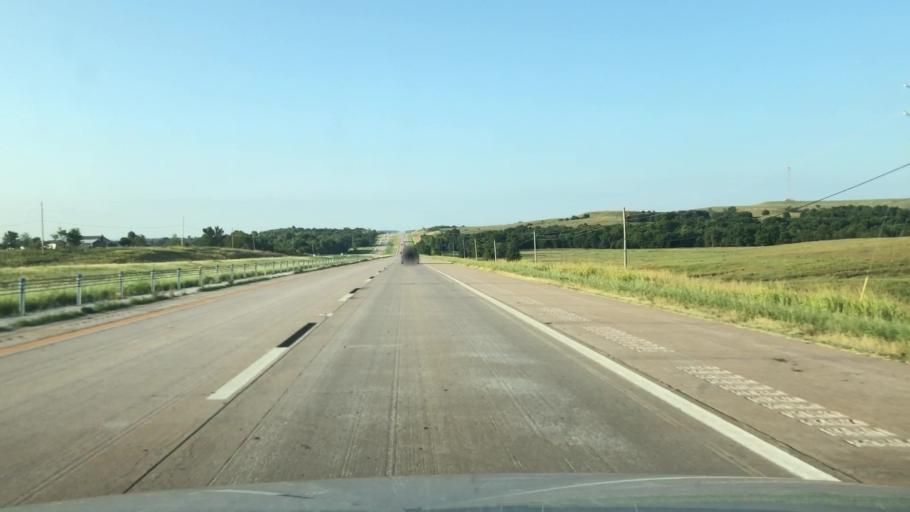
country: US
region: Oklahoma
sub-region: Osage County
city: Skiatook
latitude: 36.4941
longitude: -95.9208
